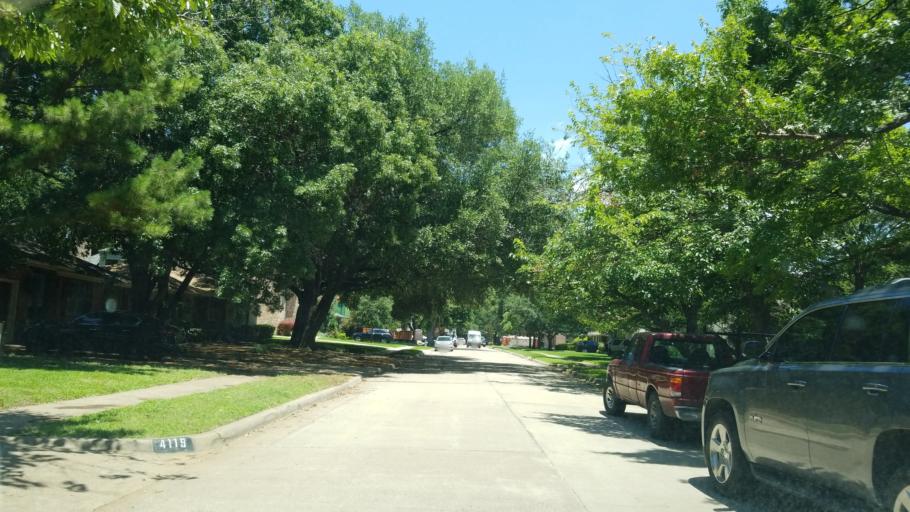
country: US
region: Texas
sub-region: Dallas County
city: University Park
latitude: 32.8762
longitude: -96.8420
